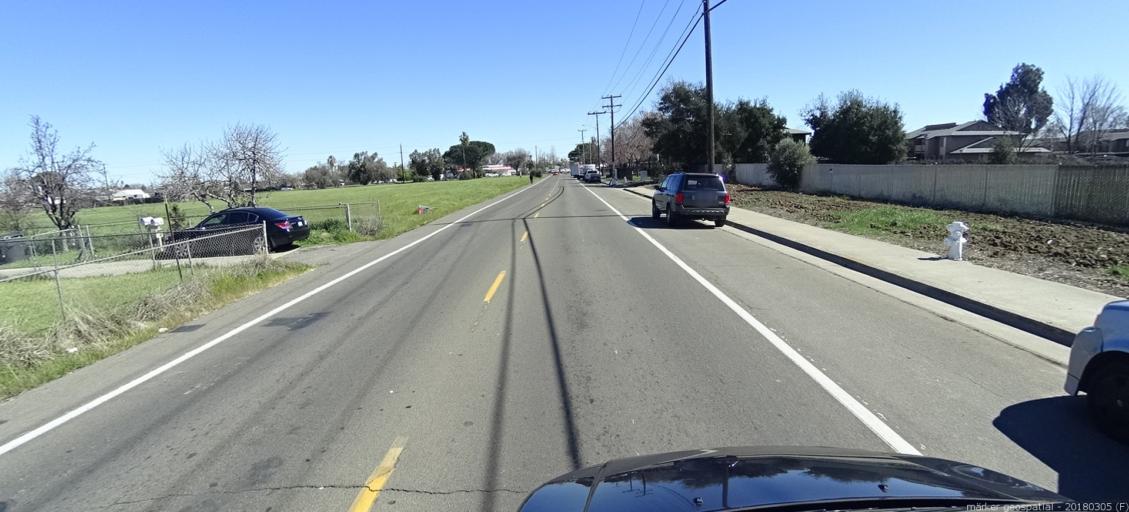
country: US
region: California
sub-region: Sacramento County
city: Florin
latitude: 38.4924
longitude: -121.4305
